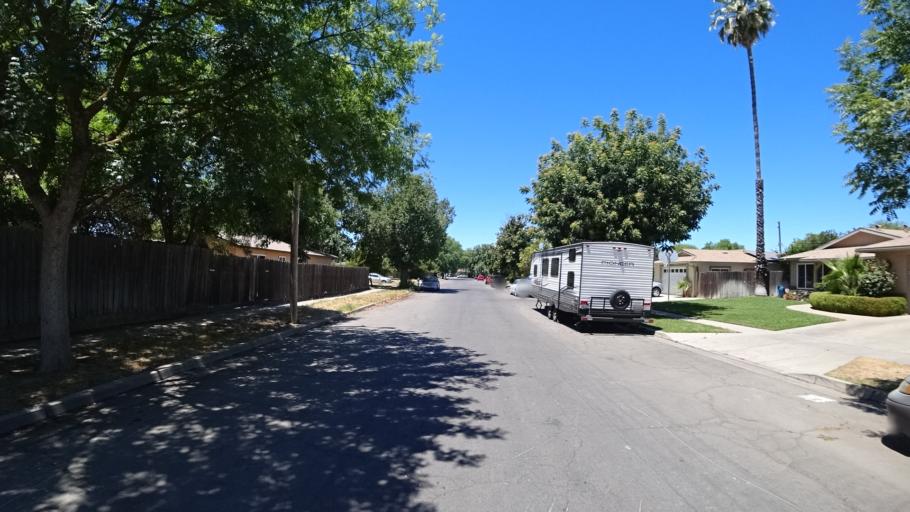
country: US
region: California
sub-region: Fresno County
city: West Park
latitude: 36.7908
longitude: -119.8468
